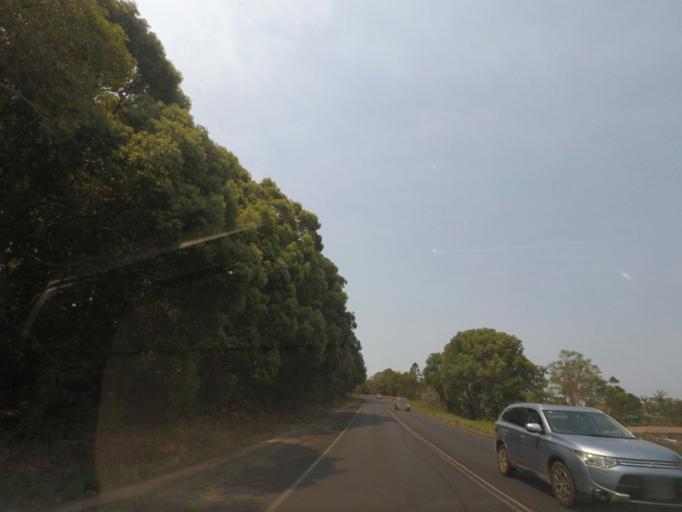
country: AU
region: New South Wales
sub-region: Byron Shire
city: Brunswick Heads
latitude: -28.5122
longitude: 153.5311
